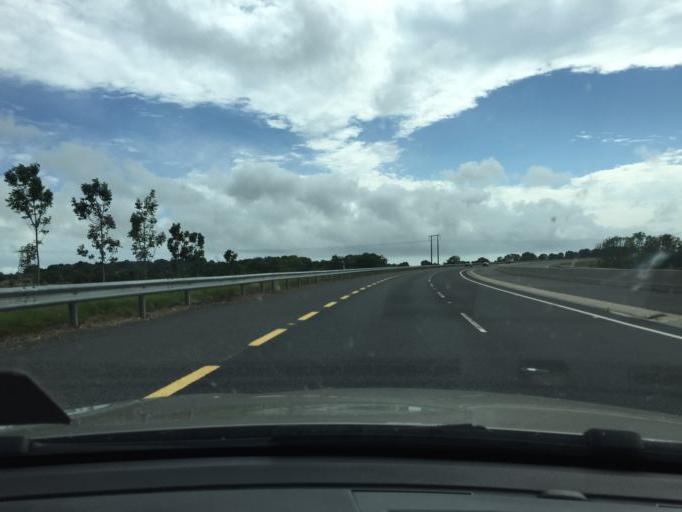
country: IE
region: Leinster
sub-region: Kilkenny
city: Mooncoin
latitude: 52.2414
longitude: -7.1893
